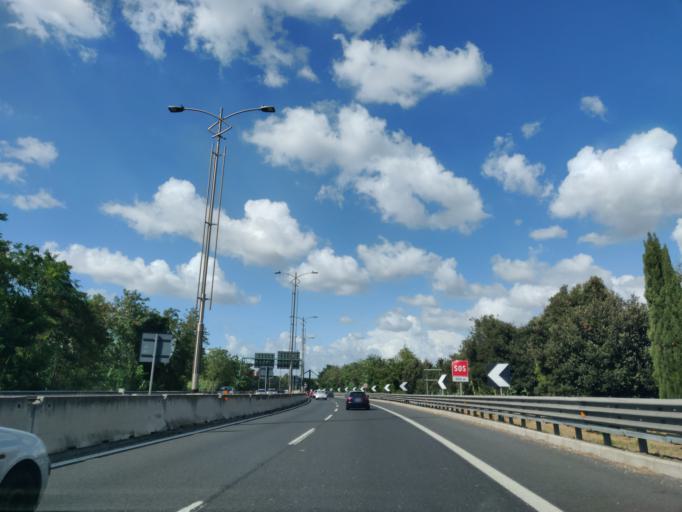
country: IT
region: Latium
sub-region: Citta metropolitana di Roma Capitale
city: Vitinia
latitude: 41.8237
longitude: 12.4191
